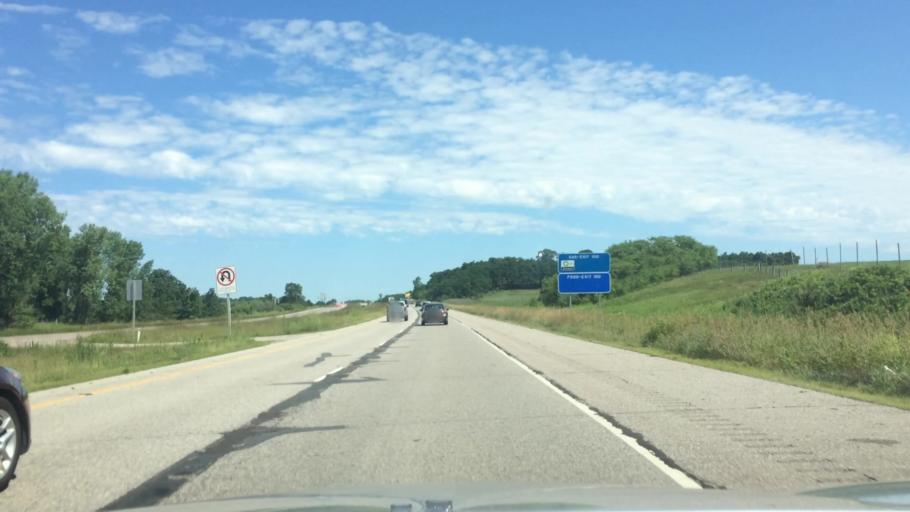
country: US
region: Wisconsin
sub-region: Columbia County
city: Portage
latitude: 43.6915
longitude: -89.4696
